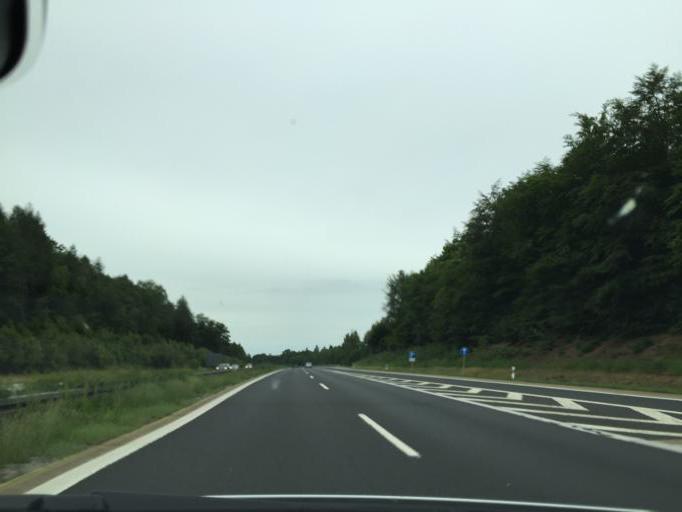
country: DE
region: Bavaria
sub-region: Regierungsbezirk Unterfranken
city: Bad Bruckenau
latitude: 50.3358
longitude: 9.7729
